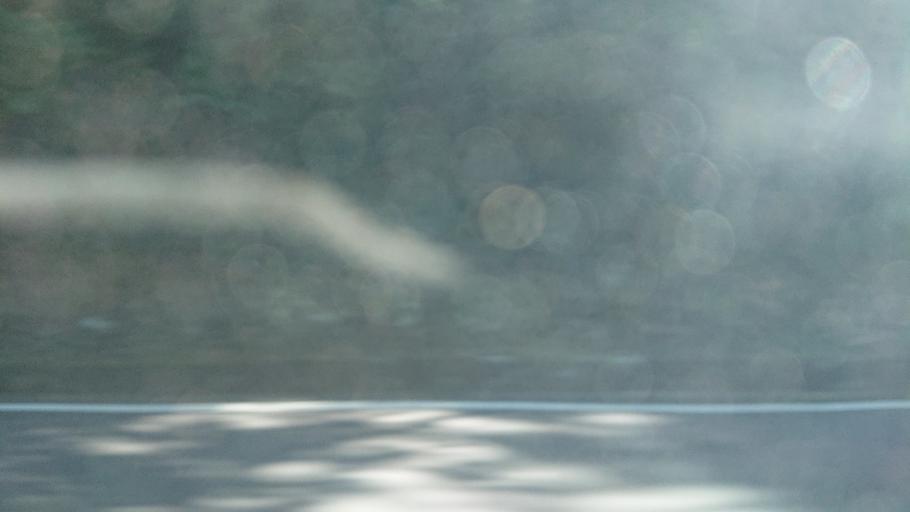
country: TW
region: Taiwan
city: Lugu
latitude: 23.4819
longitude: 120.7423
